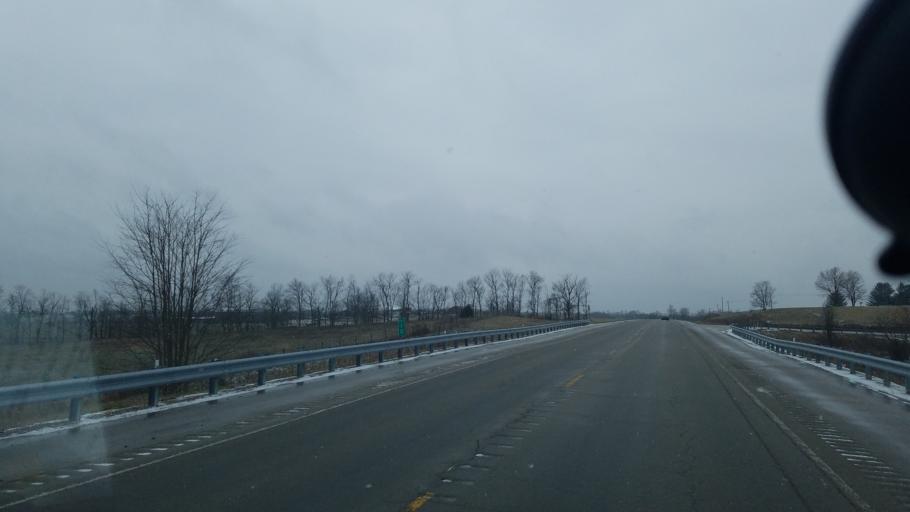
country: US
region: Kentucky
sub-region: Bath County
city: Owingsville
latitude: 38.2638
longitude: -83.8402
